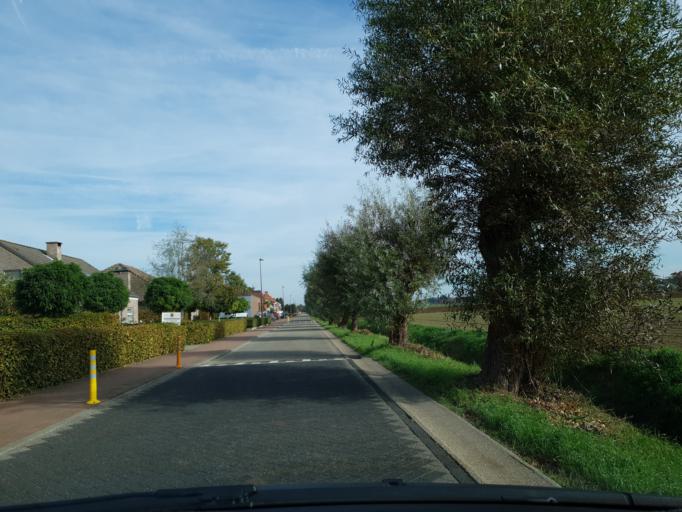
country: BE
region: Flanders
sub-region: Provincie Antwerpen
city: Stabroek
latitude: 51.3320
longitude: 4.3943
